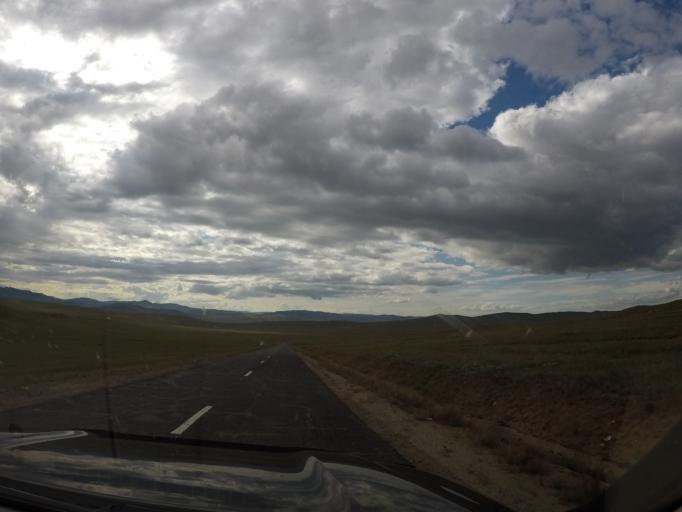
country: MN
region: Hentiy
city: Modot
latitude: 47.5910
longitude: 109.2646
